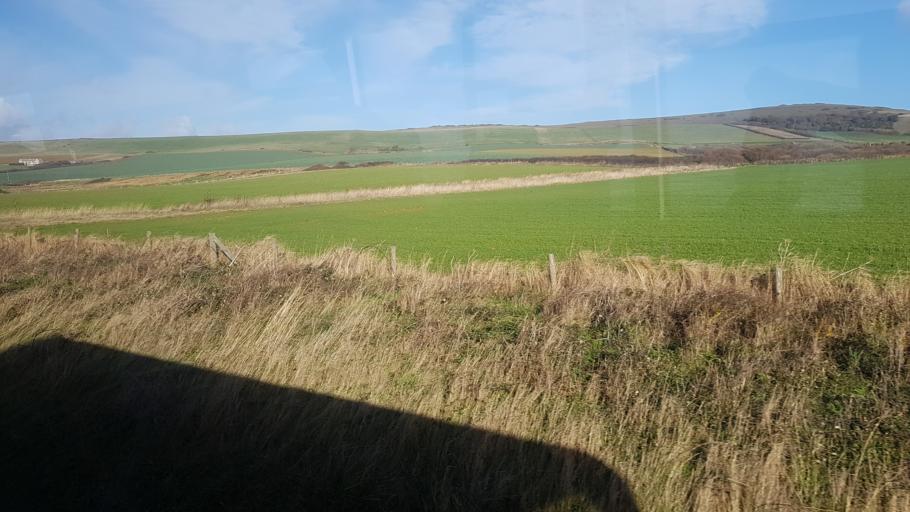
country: GB
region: England
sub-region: Isle of Wight
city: Freshwater
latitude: 50.6518
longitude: -1.4598
